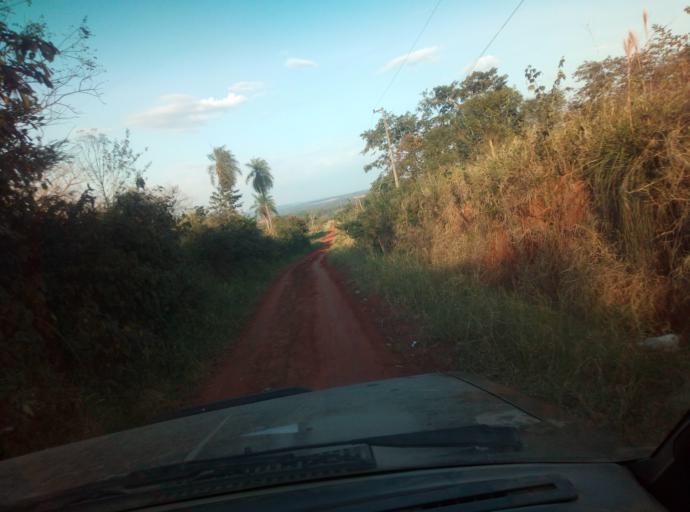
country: PY
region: Caaguazu
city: Doctor Cecilio Baez
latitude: -25.1523
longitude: -56.2454
